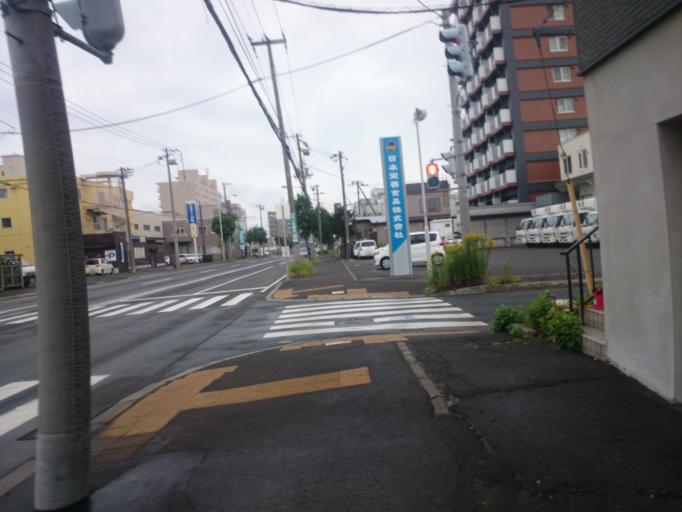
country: JP
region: Hokkaido
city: Sapporo
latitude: 43.0591
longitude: 141.3984
